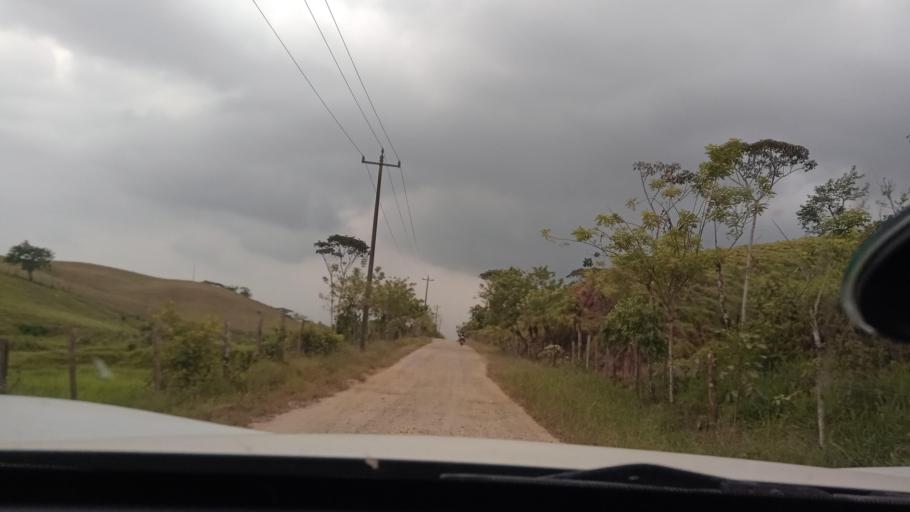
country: MX
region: Tabasco
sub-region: Huimanguillo
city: Francisco Rueda
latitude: 17.4346
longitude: -94.0516
